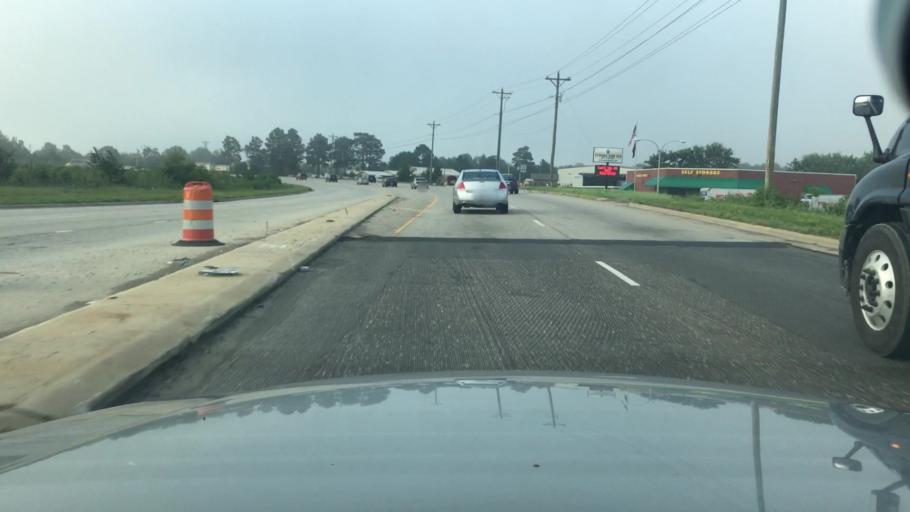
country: US
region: North Carolina
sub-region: Cumberland County
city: Hope Mills
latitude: 35.0072
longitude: -78.9187
